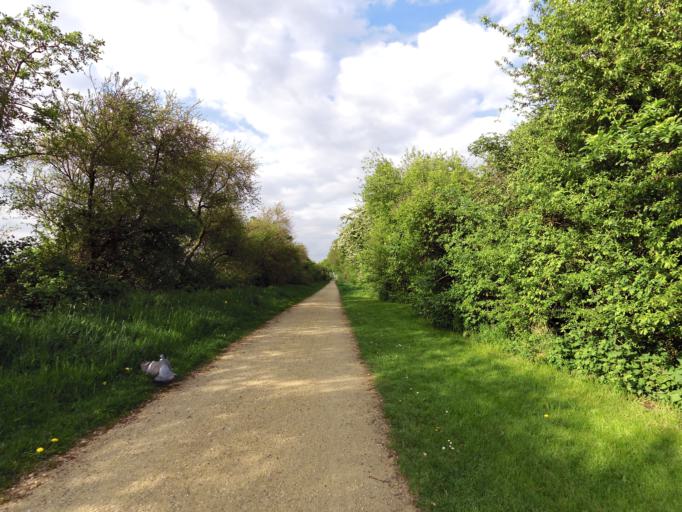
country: DE
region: North Rhine-Westphalia
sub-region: Regierungsbezirk Dusseldorf
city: Kleve
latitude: 51.8072
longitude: 6.1529
